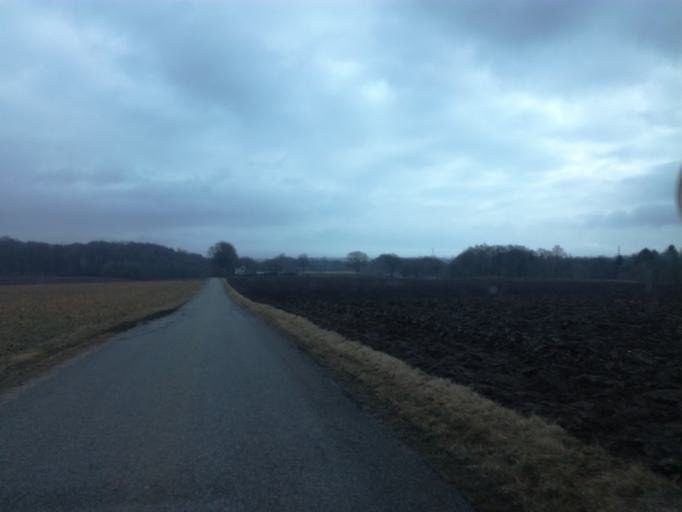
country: DK
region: South Denmark
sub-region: Vejle Kommune
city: Brejning
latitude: 55.6183
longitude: 9.6981
